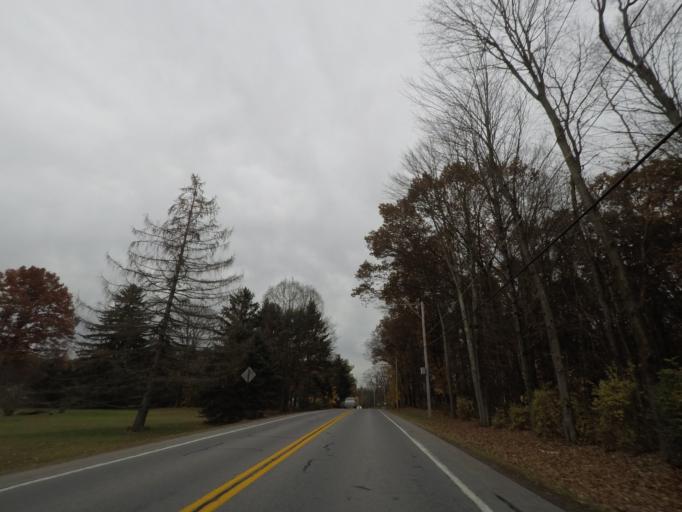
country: US
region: New York
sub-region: Schenectady County
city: Niskayuna
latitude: 42.8122
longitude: -73.8266
